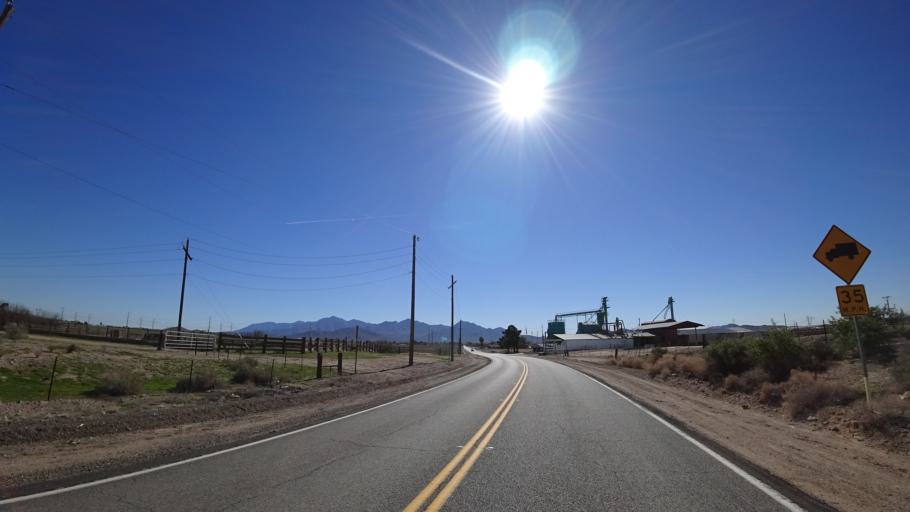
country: US
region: Arizona
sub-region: Maricopa County
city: Avondale
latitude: 33.4094
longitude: -112.3403
